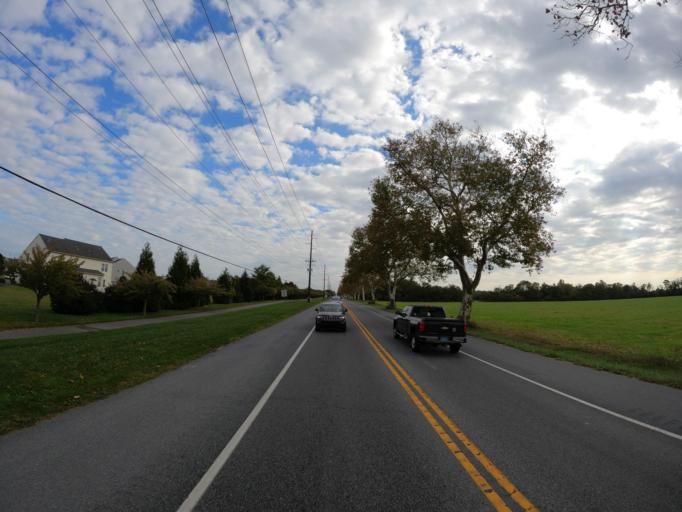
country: US
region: Delaware
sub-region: Sussex County
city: Milton
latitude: 38.7262
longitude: -75.2792
